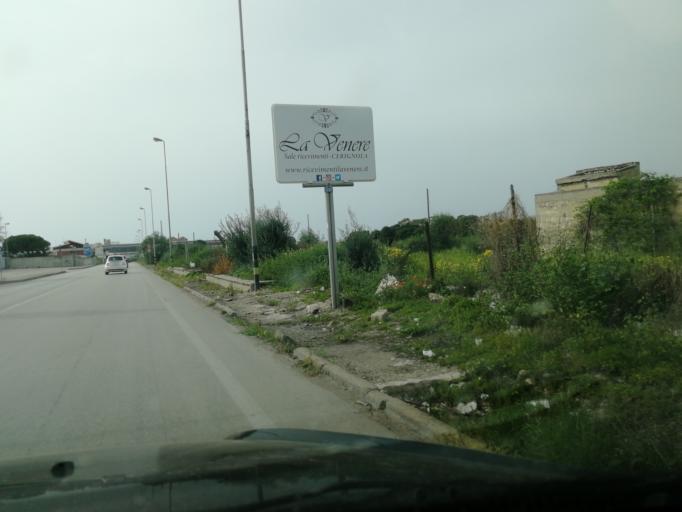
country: IT
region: Apulia
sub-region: Provincia di Barletta - Andria - Trani
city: Barletta
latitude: 41.3135
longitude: 16.3037
